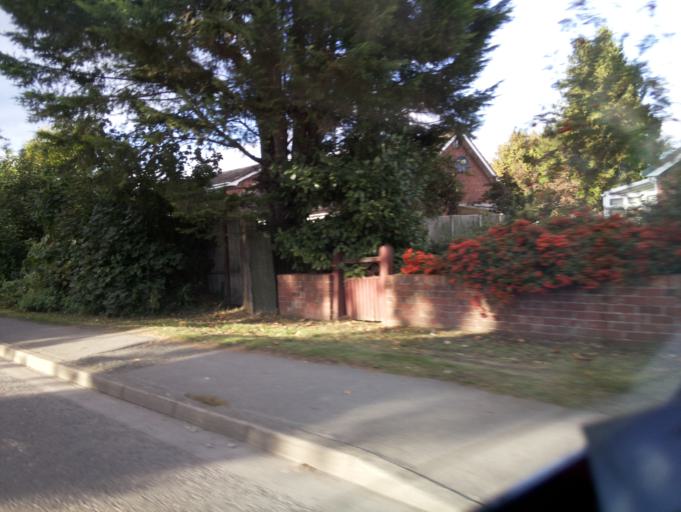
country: GB
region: England
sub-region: Herefordshire
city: Belmont
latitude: 52.0641
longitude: -2.7471
